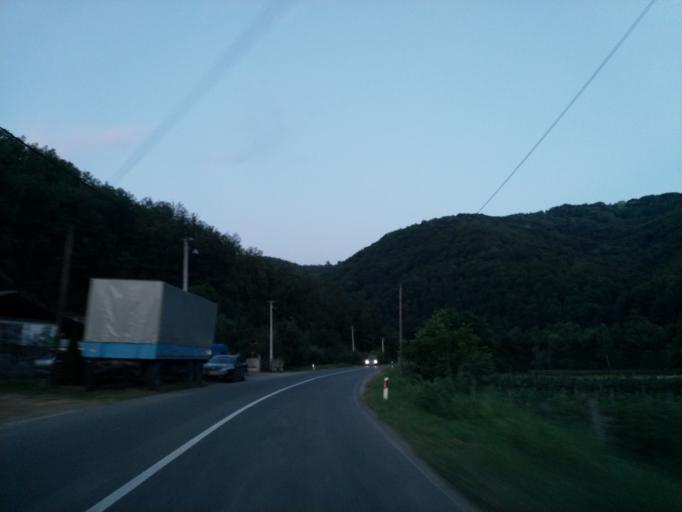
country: RS
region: Central Serbia
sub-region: Rasinski Okrug
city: Aleksandrovac
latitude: 43.3445
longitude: 21.0914
